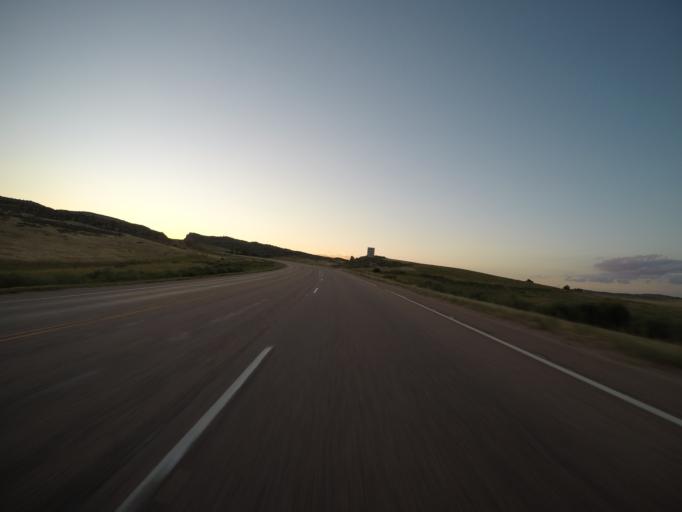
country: US
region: Colorado
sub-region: Larimer County
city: Laporte
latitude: 40.7578
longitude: -105.1716
